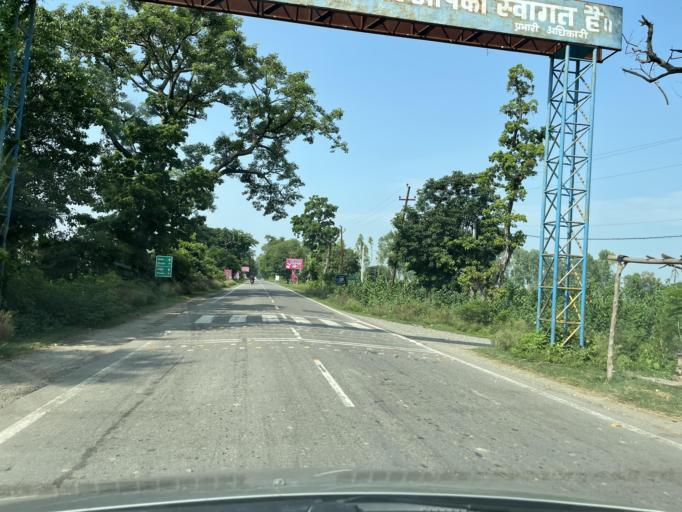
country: IN
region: Uttarakhand
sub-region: Udham Singh Nagar
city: Bazpur
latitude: 29.2158
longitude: 79.2257
